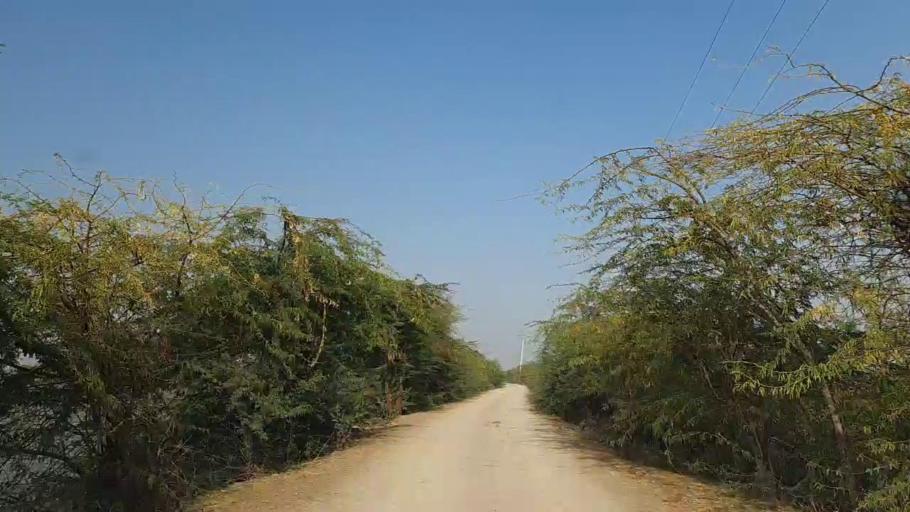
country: PK
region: Sindh
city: Jati
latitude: 24.5226
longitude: 68.2637
